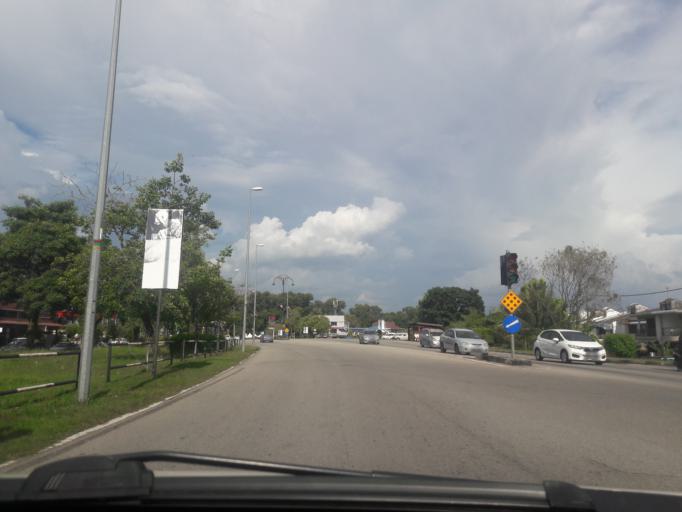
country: MY
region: Kedah
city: Sungai Petani
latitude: 5.6516
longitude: 100.5059
